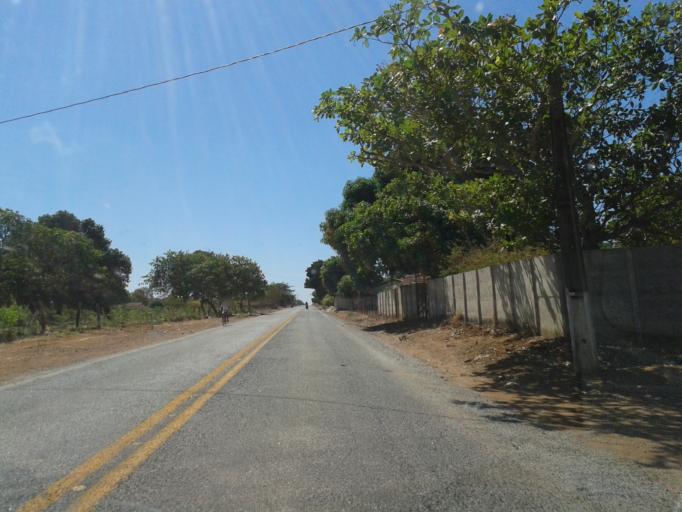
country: BR
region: Goias
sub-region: Sao Miguel Do Araguaia
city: Sao Miguel do Araguaia
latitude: -13.2644
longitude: -50.1500
